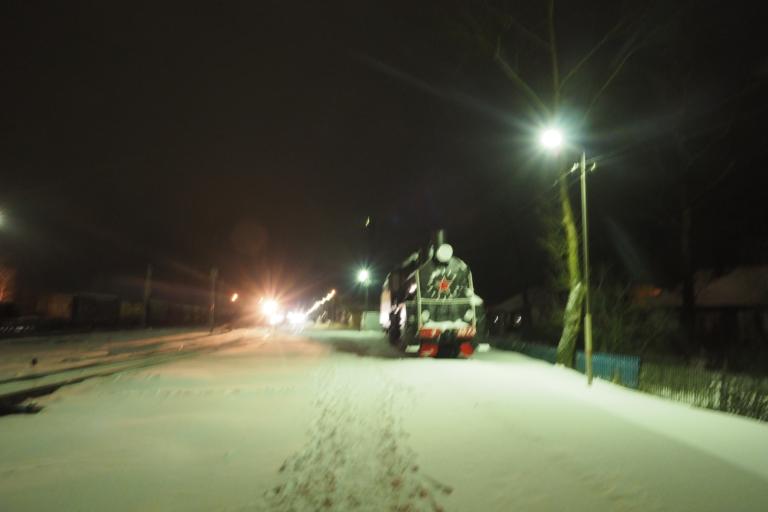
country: RU
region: Tverskaya
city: Sonkovo
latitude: 57.7802
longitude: 37.1649
